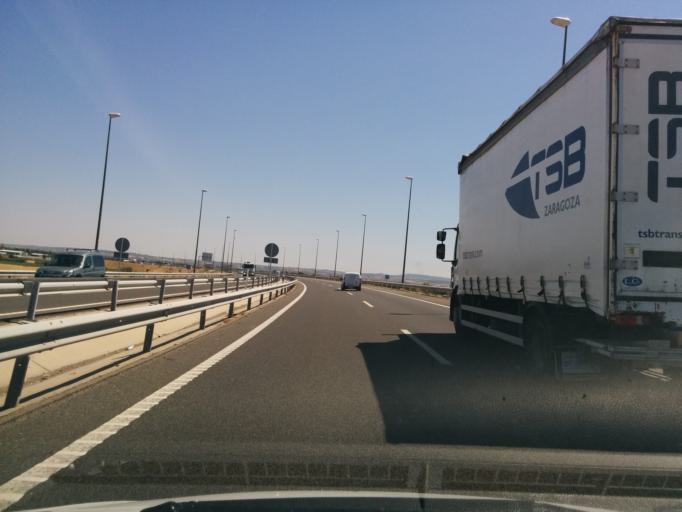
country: ES
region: Aragon
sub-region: Provincia de Zaragoza
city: Zaragoza
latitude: 41.6551
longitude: -0.8410
